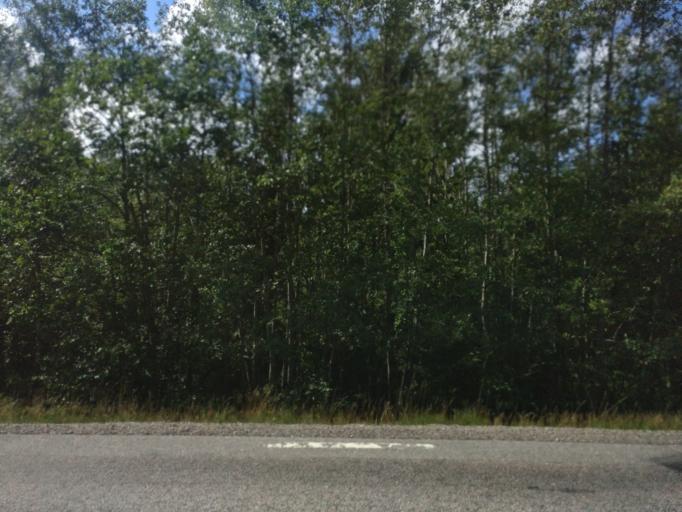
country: SE
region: Vaermland
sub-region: Hagfors Kommun
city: Ekshaerad
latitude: 60.3714
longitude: 13.3035
